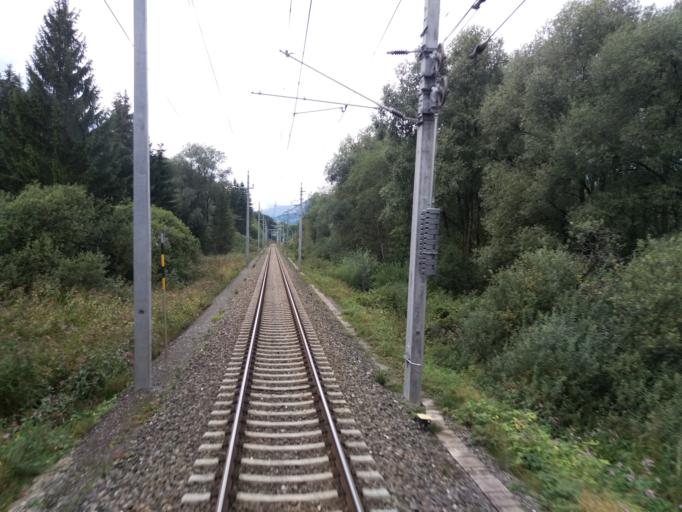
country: AT
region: Styria
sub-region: Politischer Bezirk Liezen
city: Lassing
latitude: 47.5500
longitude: 14.2671
